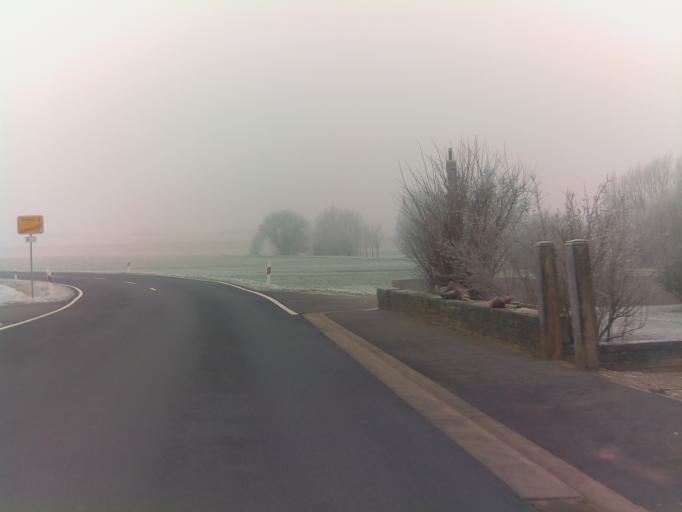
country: DE
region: Bavaria
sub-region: Regierungsbezirk Unterfranken
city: Lulsfeld
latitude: 49.8670
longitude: 10.3160
